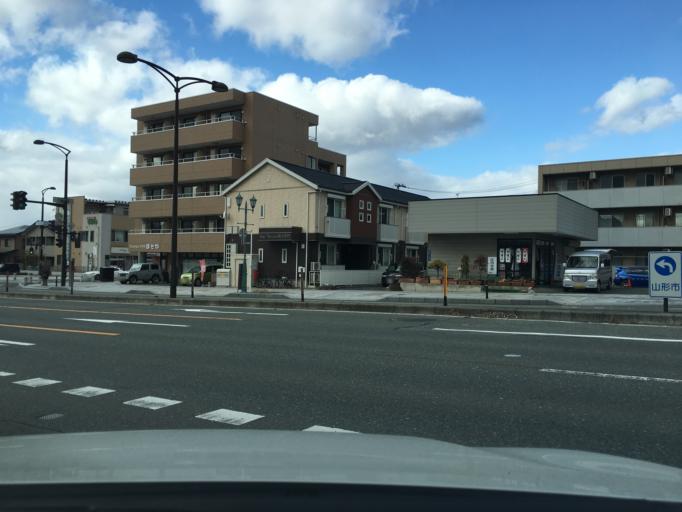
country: JP
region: Yamagata
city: Yamagata-shi
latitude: 38.2518
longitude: 140.3269
